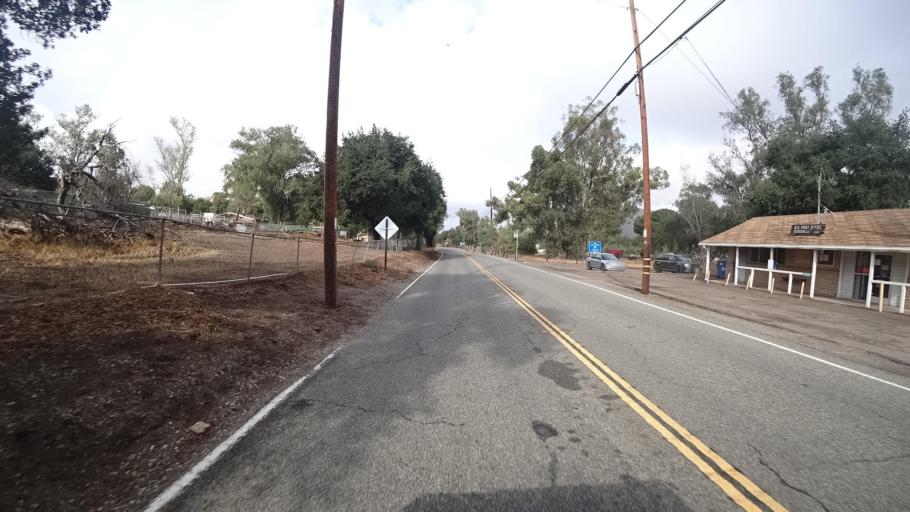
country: MX
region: Baja California
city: Tecate
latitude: 32.6048
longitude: -116.6104
